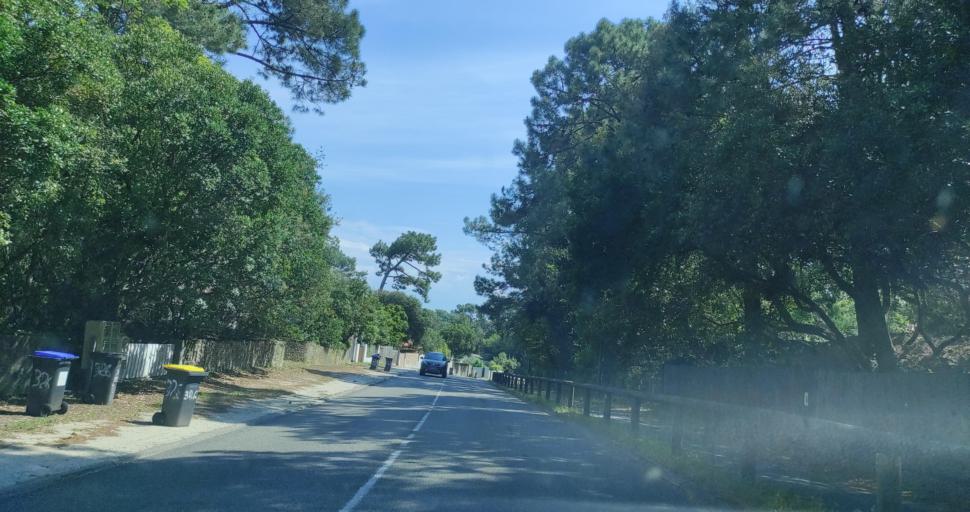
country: FR
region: Aquitaine
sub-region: Departement de la Gironde
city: Arcachon
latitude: 44.6884
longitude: -1.2392
